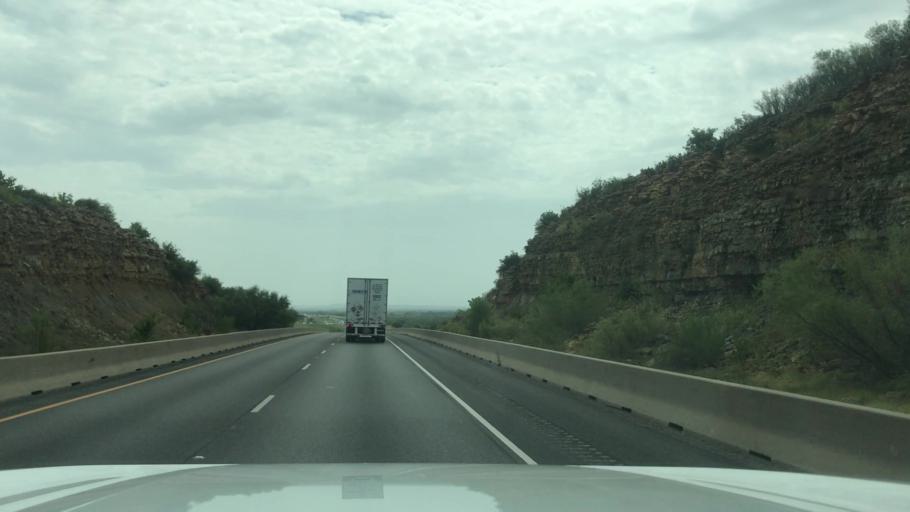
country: US
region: Texas
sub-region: Callahan County
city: Baird
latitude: 32.3948
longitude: -99.3615
